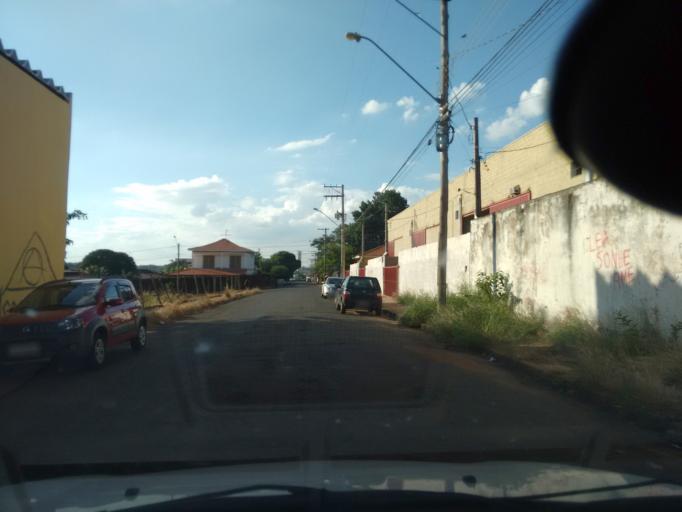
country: BR
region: Sao Paulo
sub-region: Araraquara
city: Araraquara
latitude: -21.8024
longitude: -48.1934
